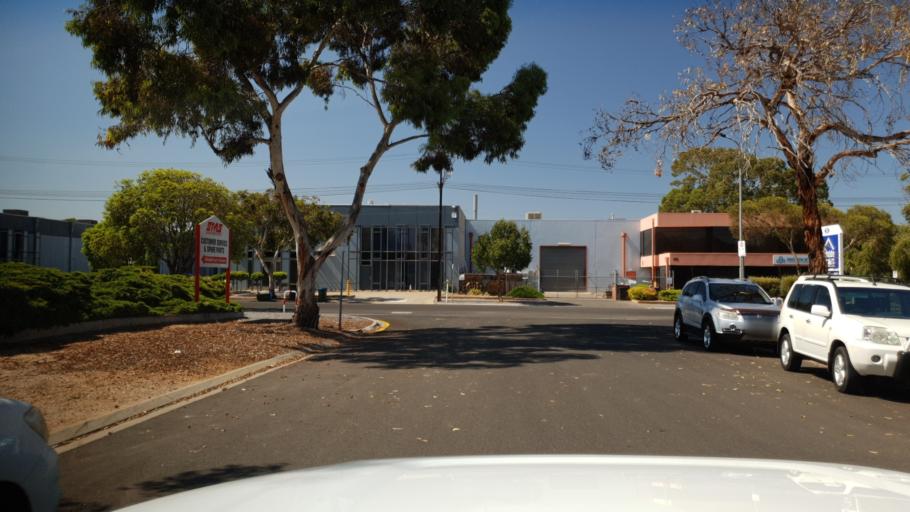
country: AU
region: South Australia
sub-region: Marion
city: Clovelly Park
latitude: -34.9903
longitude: 138.5792
